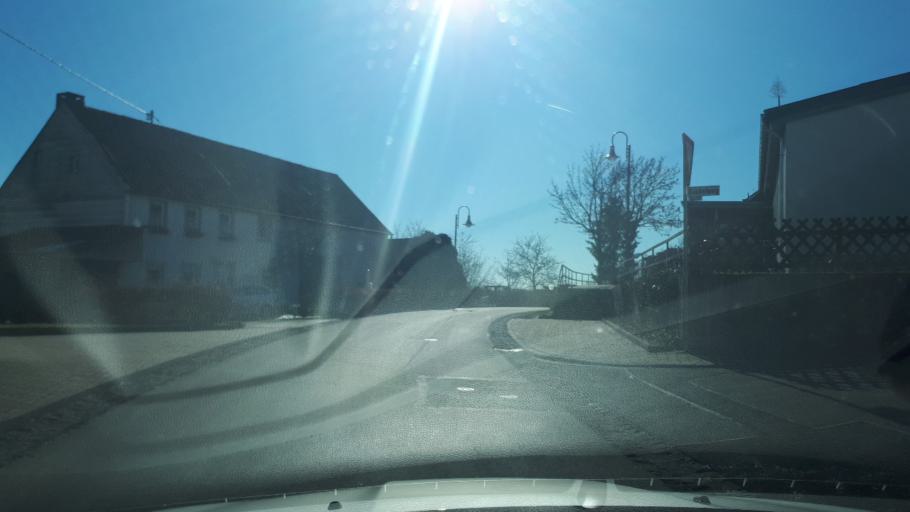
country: DE
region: Rheinland-Pfalz
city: Ellscheid
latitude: 50.1493
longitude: 6.9147
